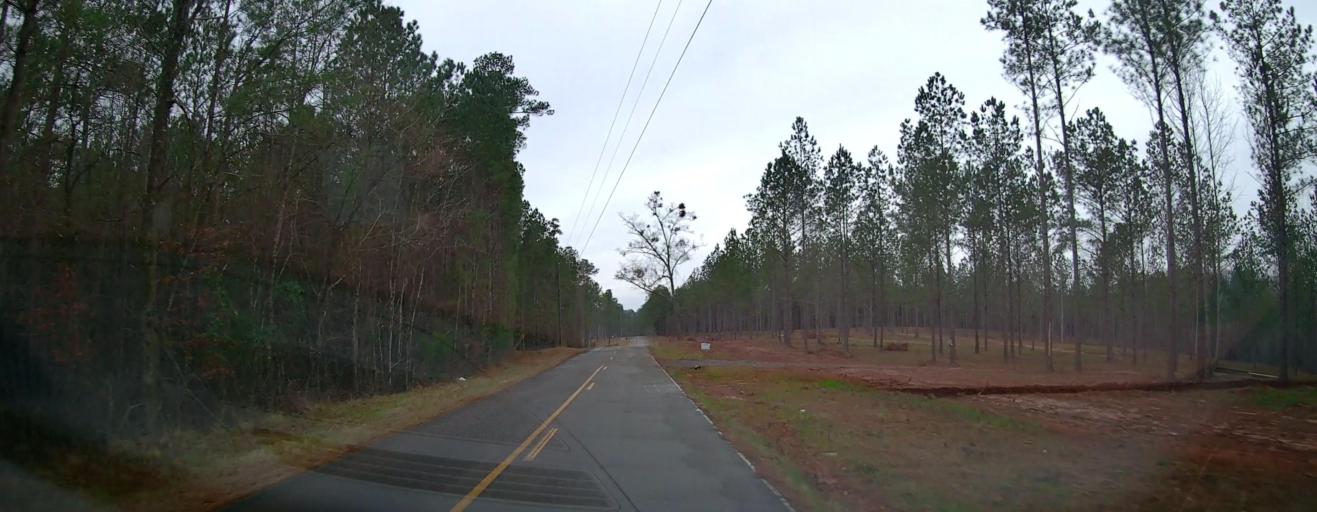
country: US
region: Georgia
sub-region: Monroe County
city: Forsyth
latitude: 33.0164
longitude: -83.8346
